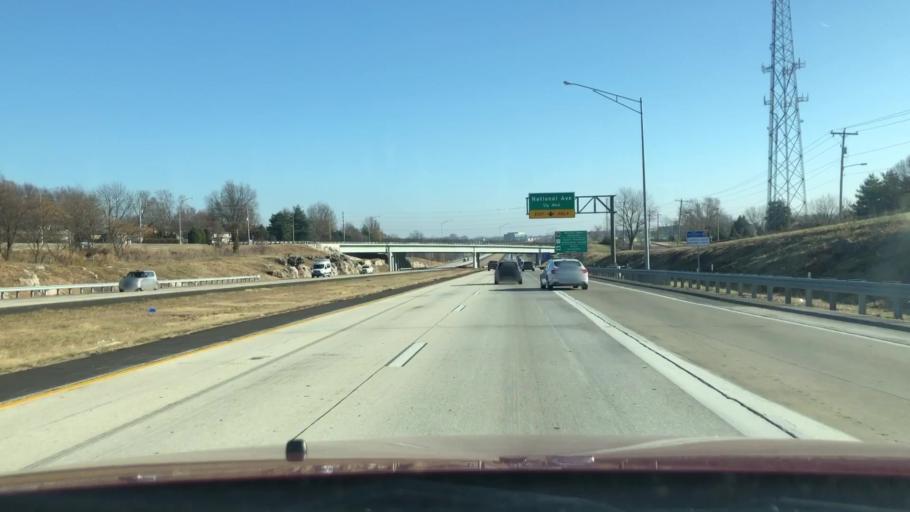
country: US
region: Missouri
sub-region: Greene County
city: Springfield
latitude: 37.1376
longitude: -93.2919
